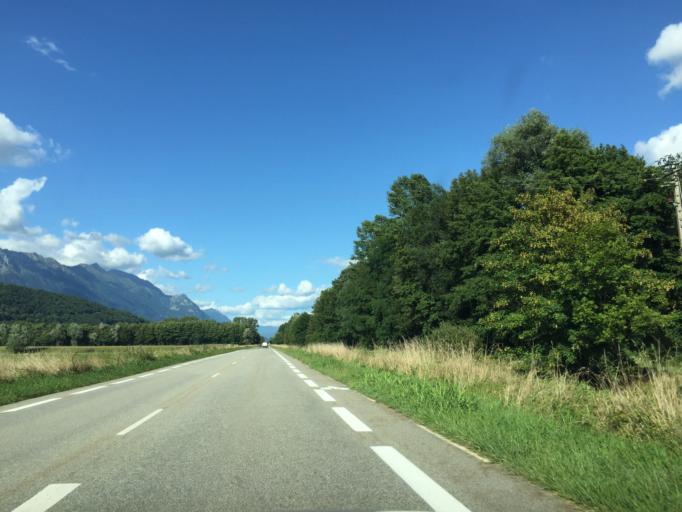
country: FR
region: Rhone-Alpes
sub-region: Departement de la Savoie
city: Coise-Saint-Jean-Pied-Gauthier
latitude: 45.5003
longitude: 6.1629
